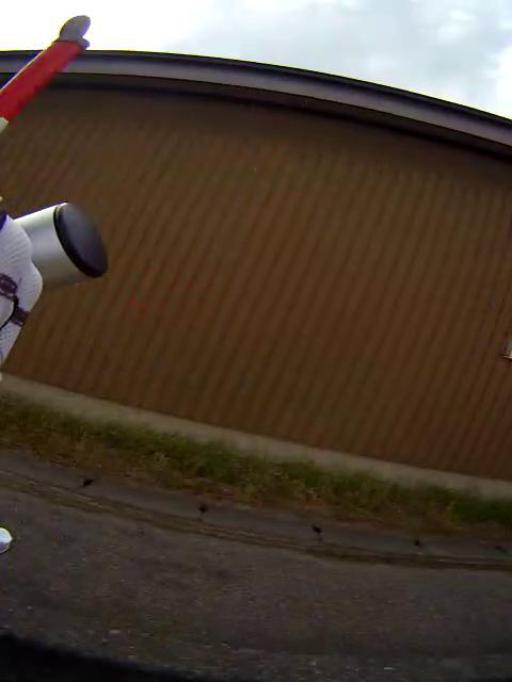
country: JP
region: Toyama
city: Takaoka
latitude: 36.7138
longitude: 136.9902
